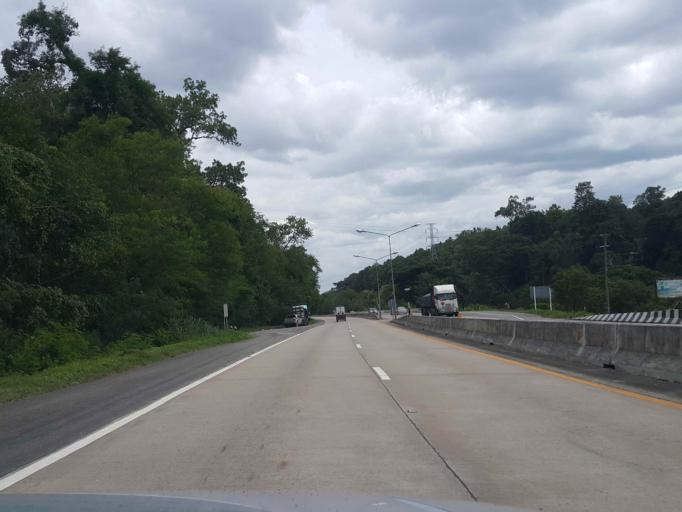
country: TH
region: Lampang
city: Hang Chat
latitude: 18.3713
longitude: 99.2359
